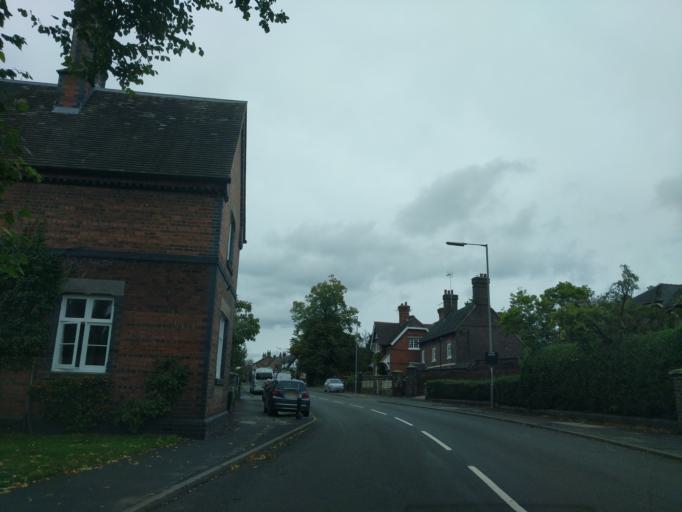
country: GB
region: England
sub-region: Cheshire East
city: Chorlton
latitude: 53.0329
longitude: -2.3682
